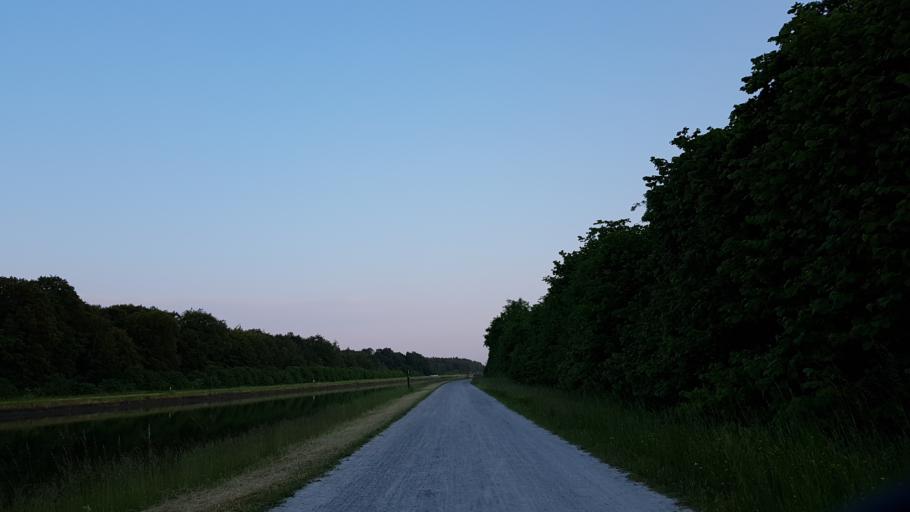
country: DE
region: Lower Saxony
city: Scharnebeck
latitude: 53.2840
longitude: 10.4865
